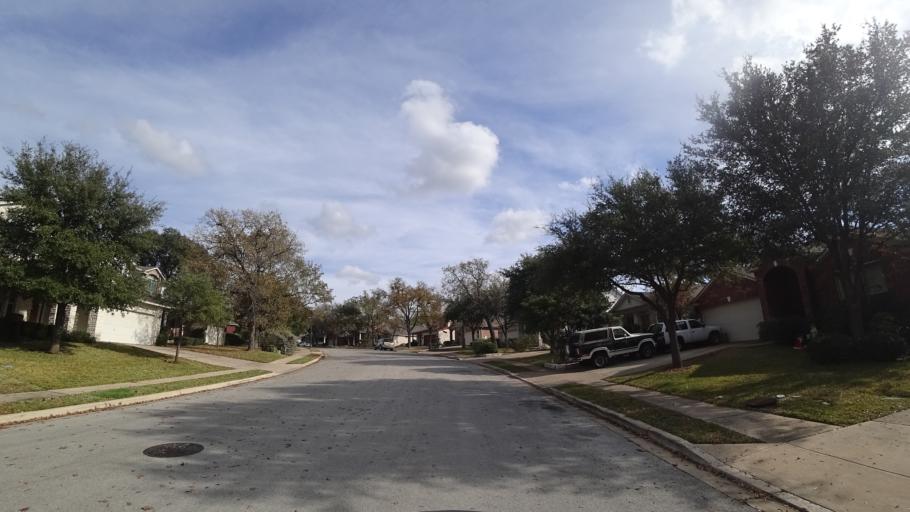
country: US
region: Texas
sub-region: Williamson County
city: Brushy Creek
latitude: 30.5056
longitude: -97.7475
